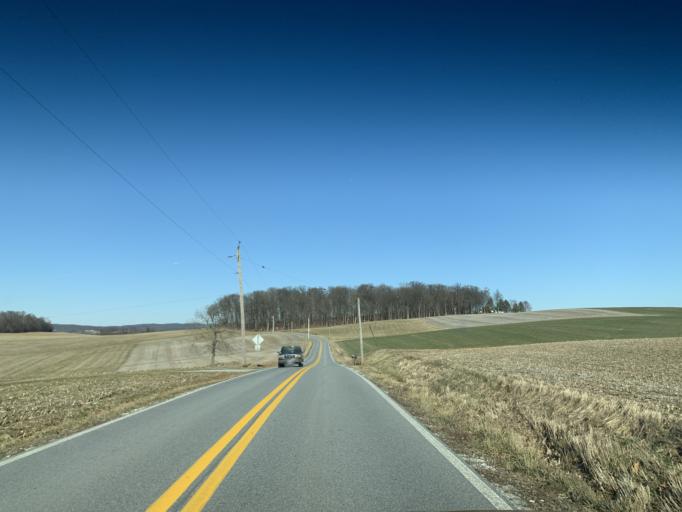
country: US
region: Maryland
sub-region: Carroll County
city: Westminster
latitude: 39.6335
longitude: -76.9717
